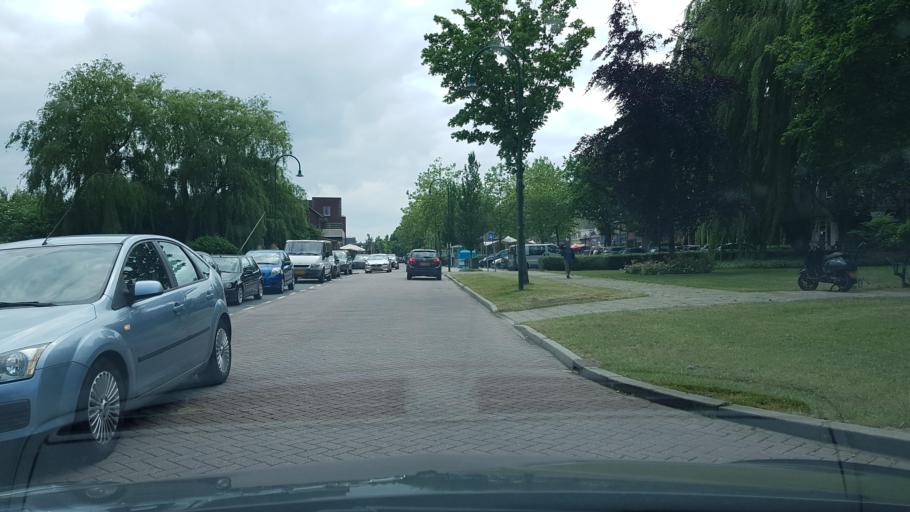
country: NL
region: Utrecht
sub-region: Stichtse Vecht
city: Vreeland
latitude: 52.2651
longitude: 5.0456
